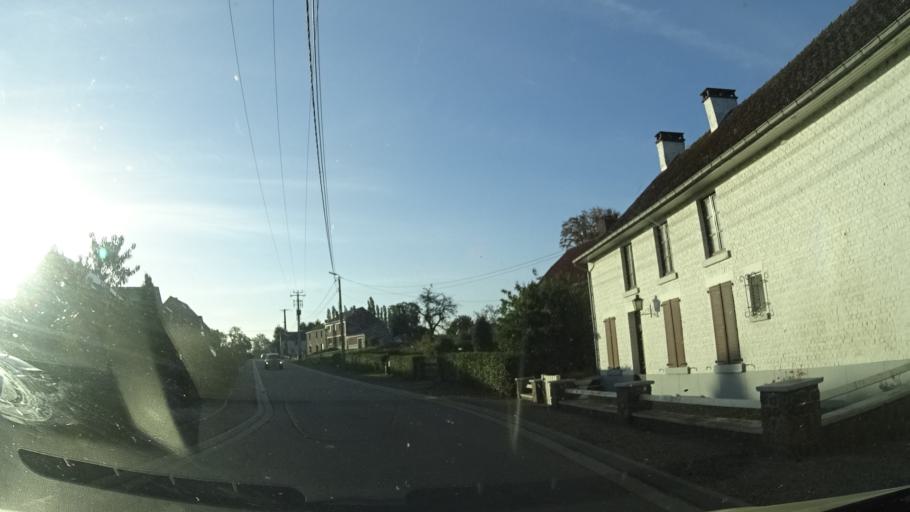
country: BE
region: Wallonia
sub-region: Province du Hainaut
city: Beaumont
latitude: 50.2616
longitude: 4.2322
